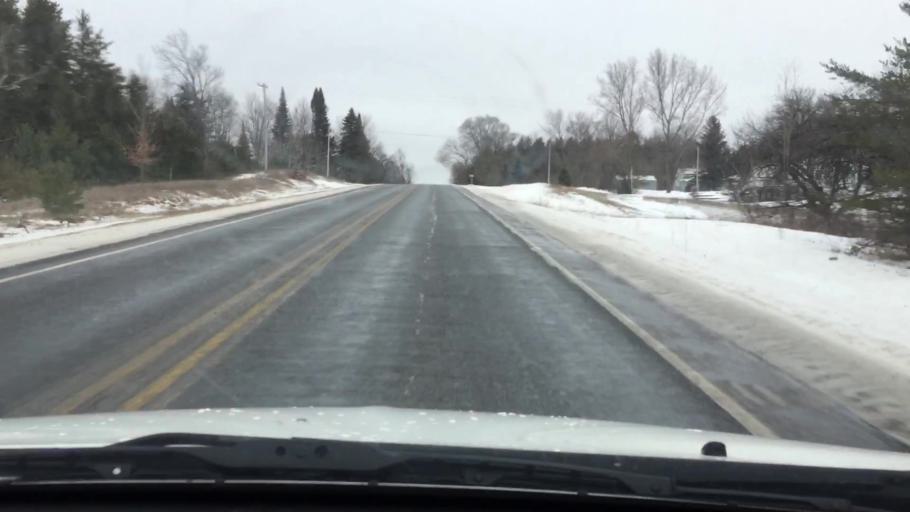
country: US
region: Michigan
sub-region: Wexford County
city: Cadillac
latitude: 44.0938
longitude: -85.4442
